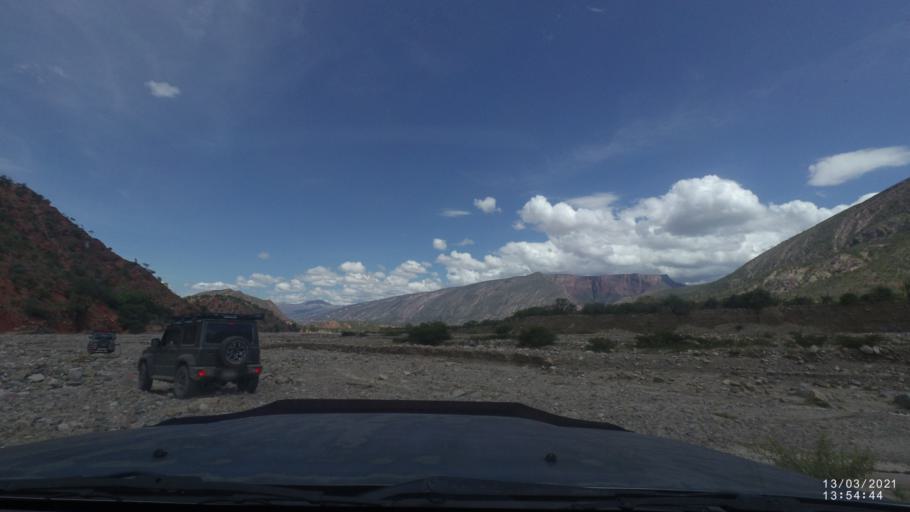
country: BO
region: Cochabamba
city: Cliza
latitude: -17.9341
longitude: -65.8660
